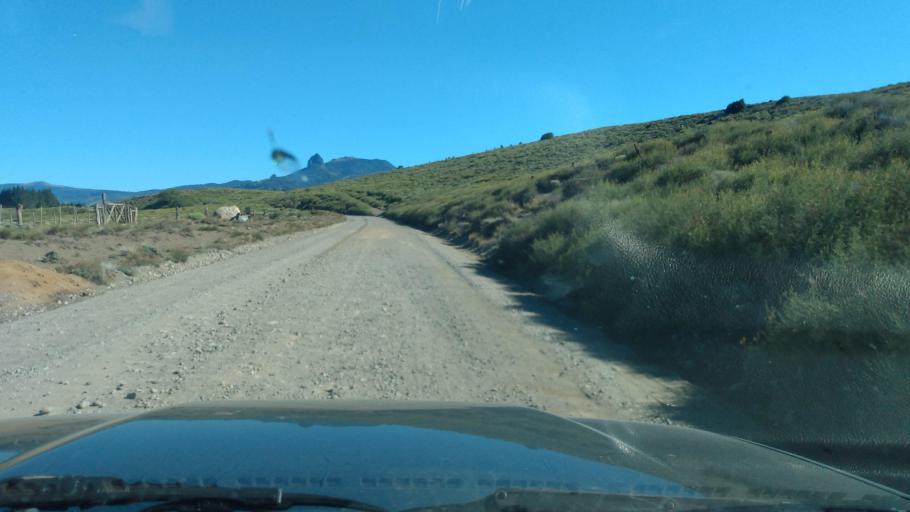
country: AR
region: Neuquen
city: Junin de los Andes
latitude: -39.8082
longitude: -71.2071
